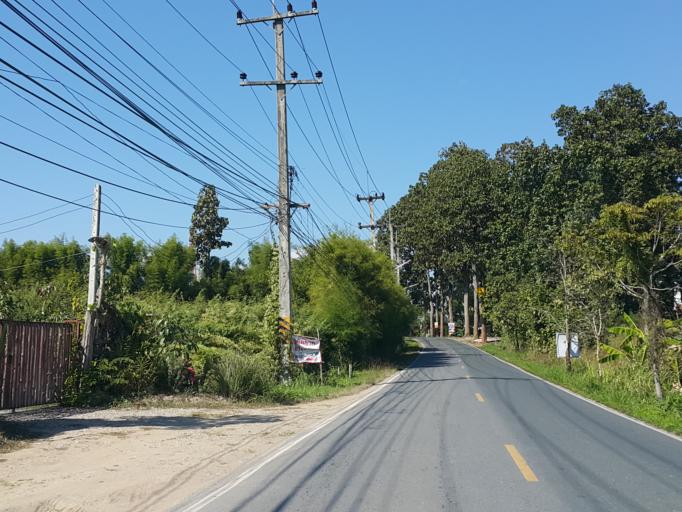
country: TH
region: Chiang Mai
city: San Sai
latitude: 18.9549
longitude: 98.9233
